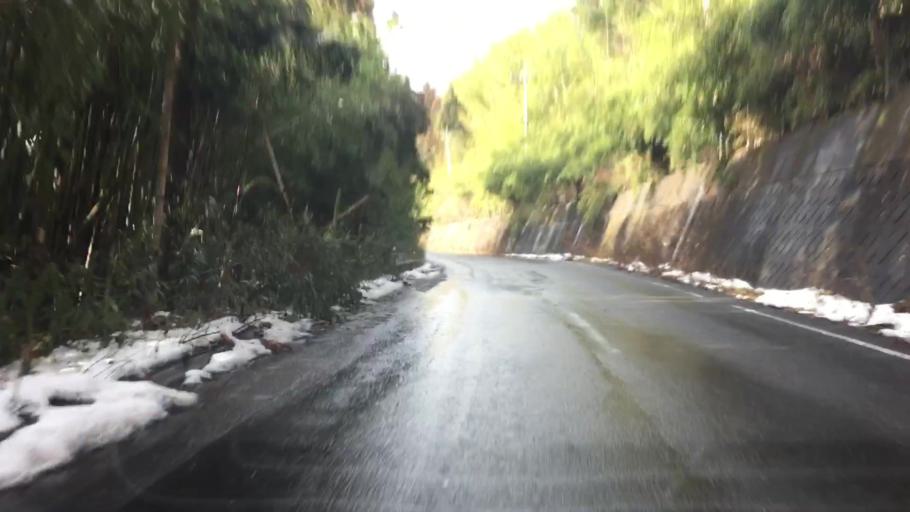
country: JP
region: Gunma
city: Numata
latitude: 36.6577
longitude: 139.0861
